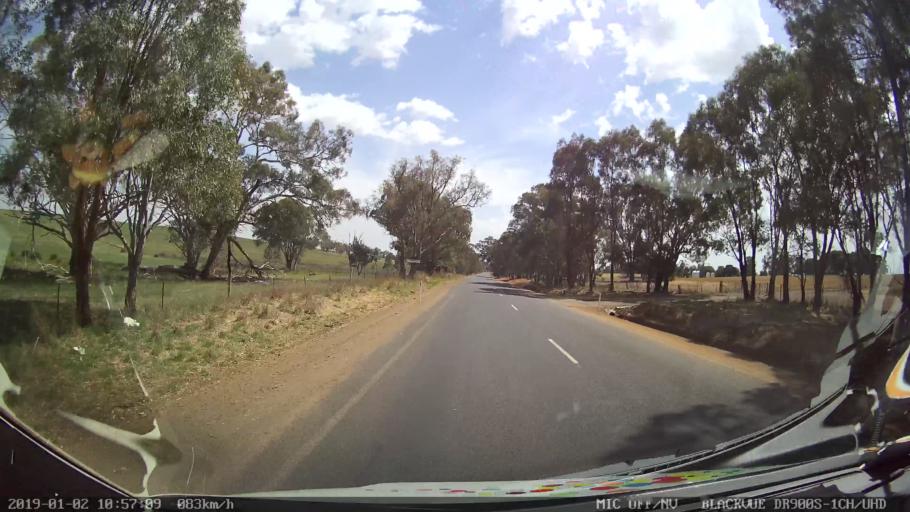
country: AU
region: New South Wales
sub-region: Cootamundra
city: Cootamundra
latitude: -34.6388
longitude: 148.2809
